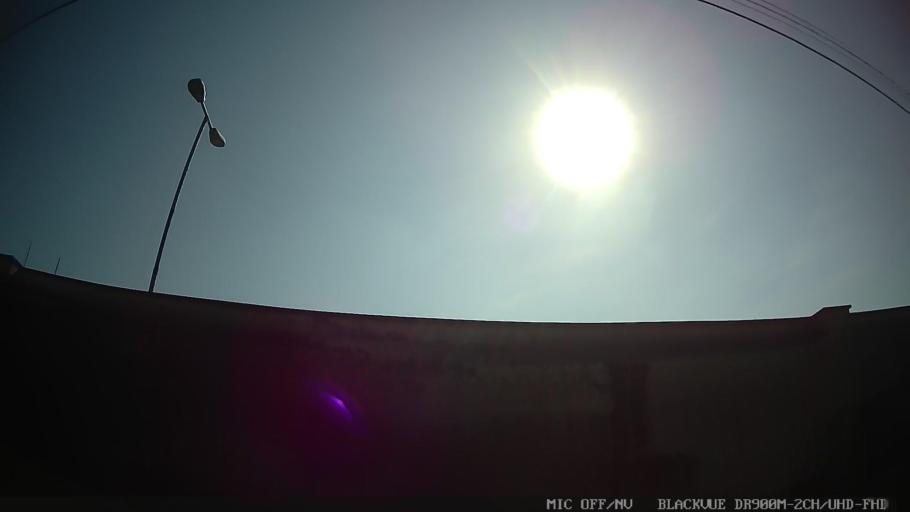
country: BR
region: Sao Paulo
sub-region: Guaruja
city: Guaruja
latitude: -24.0057
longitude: -46.2969
